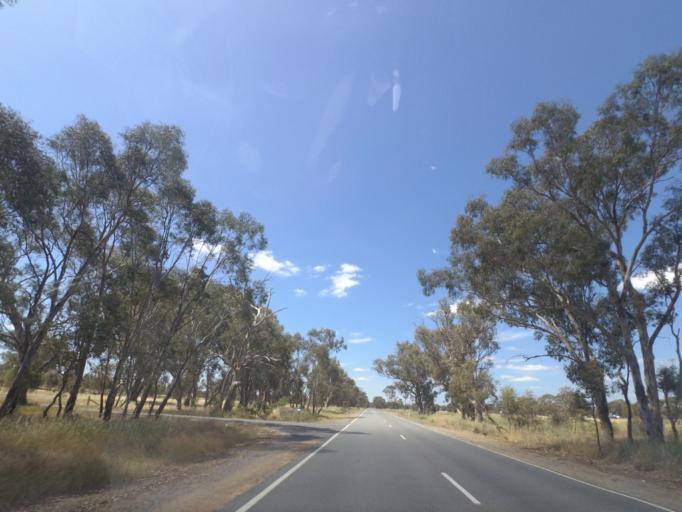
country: AU
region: Victoria
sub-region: Wangaratta
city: Wangaratta
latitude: -36.4199
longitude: 146.2620
